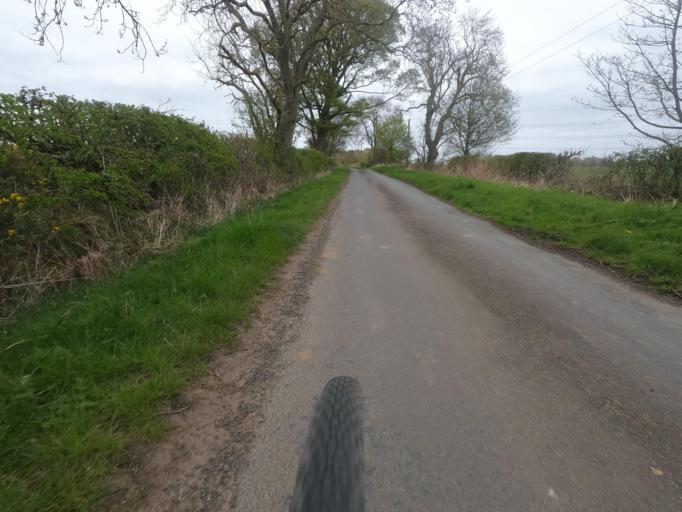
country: GB
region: England
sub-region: Northumberland
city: Horsley
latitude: 55.0619
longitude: -1.8438
